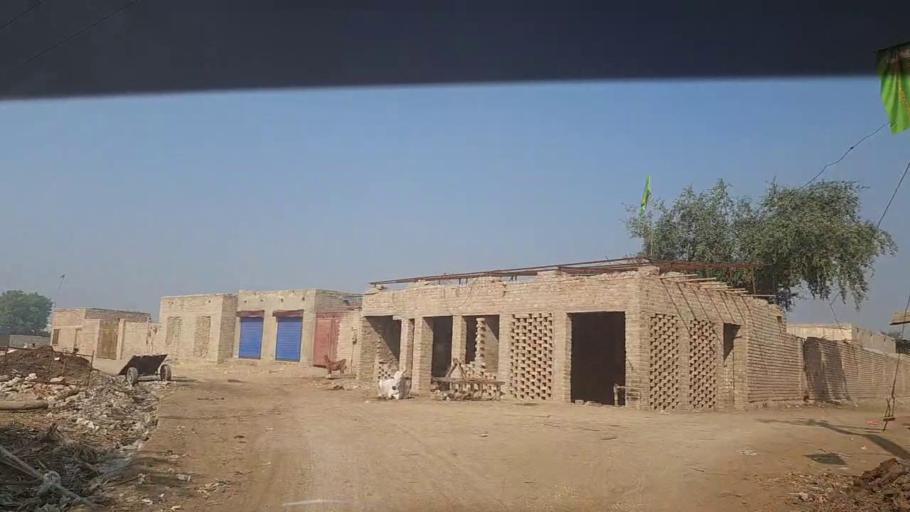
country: PK
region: Sindh
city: Khairpur
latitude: 27.4720
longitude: 68.7125
